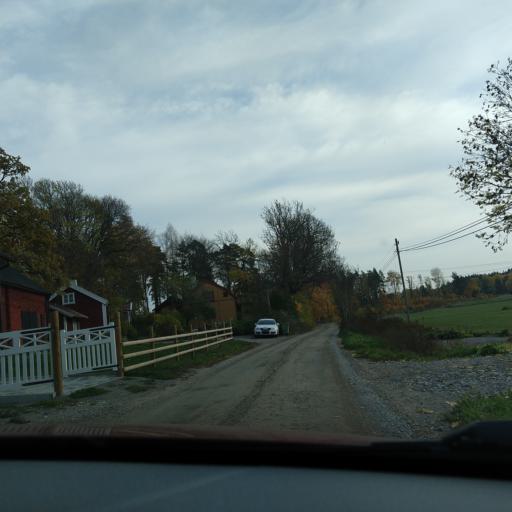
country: SE
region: Stockholm
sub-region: Vallentuna Kommun
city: Vallentuna
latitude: 59.5241
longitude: 18.0199
